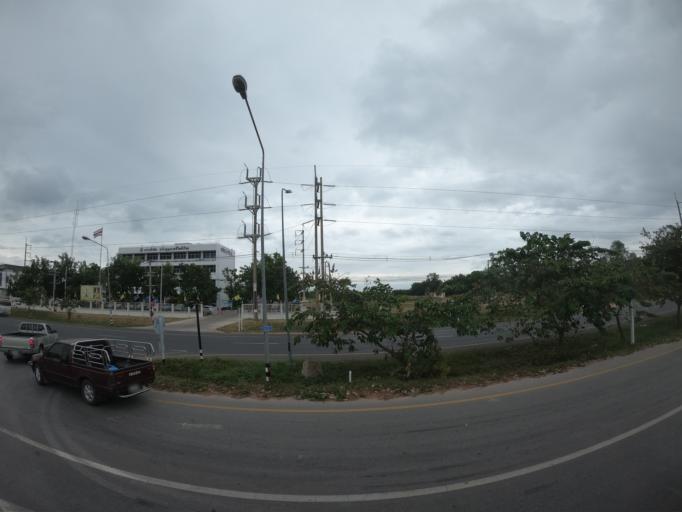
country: TH
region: Roi Et
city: Roi Et
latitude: 16.0447
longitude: 103.6270
